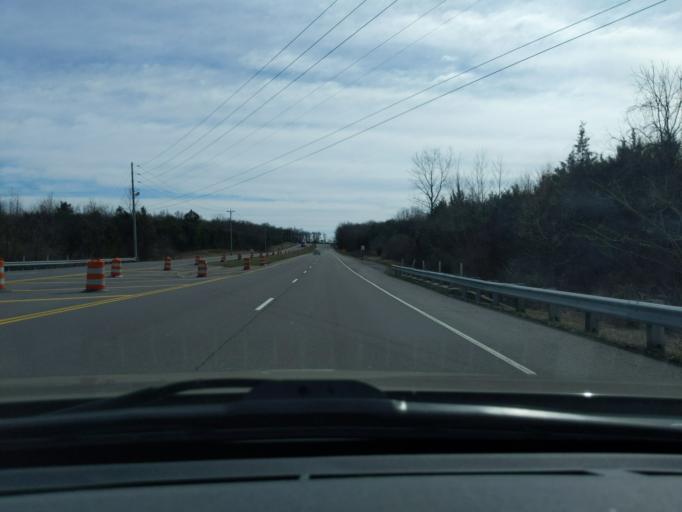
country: US
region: Tennessee
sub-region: Wilson County
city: Mount Juliet
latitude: 36.1853
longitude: -86.4631
